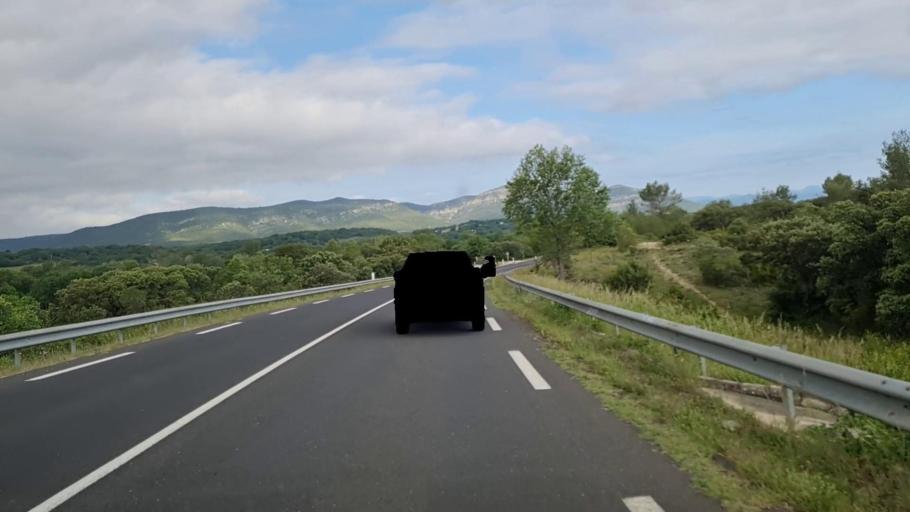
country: FR
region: Languedoc-Roussillon
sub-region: Departement du Gard
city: Quissac
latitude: 43.8858
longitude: 4.0186
